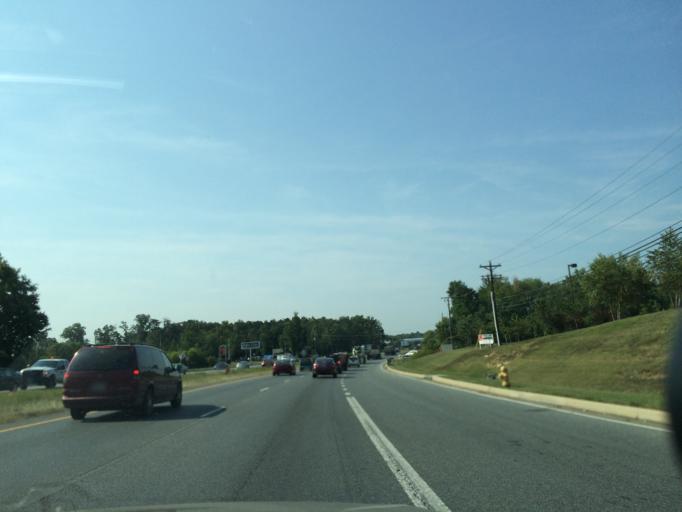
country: US
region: Maryland
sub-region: Charles County
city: Saint Charles
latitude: 38.5966
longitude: -76.9381
